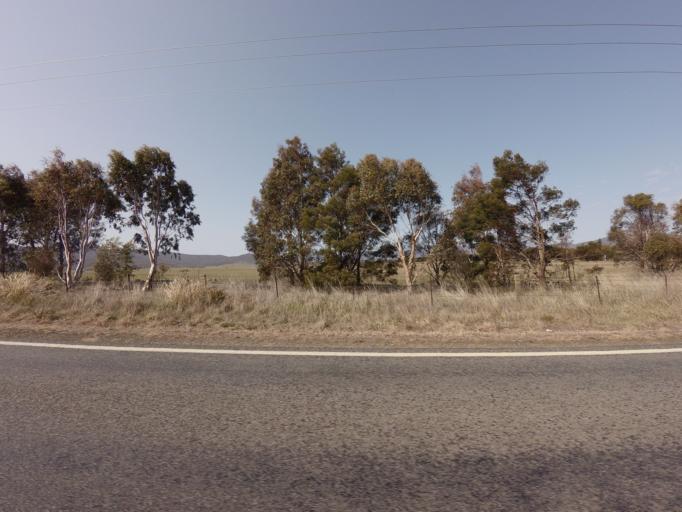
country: AU
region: Tasmania
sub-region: Northern Midlands
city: Evandale
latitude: -41.7938
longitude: 147.7093
